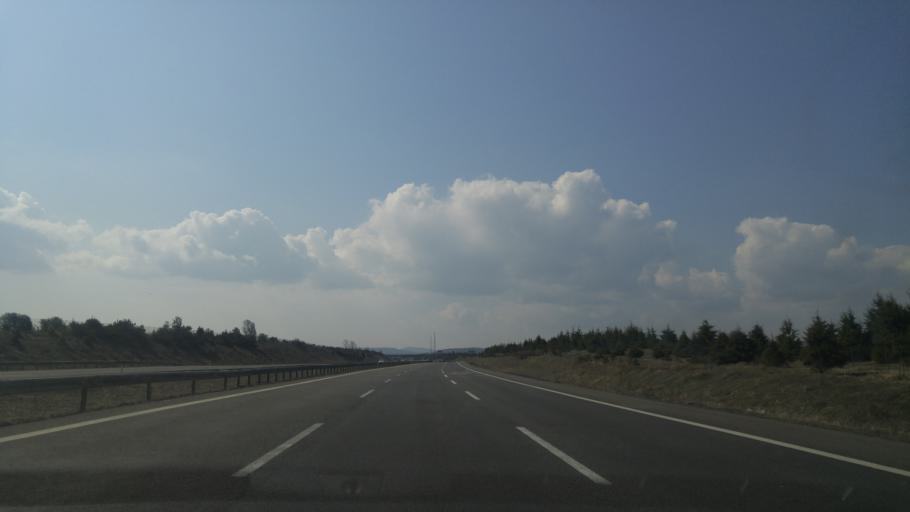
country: TR
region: Bolu
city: Gerede
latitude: 40.7070
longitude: 32.2231
